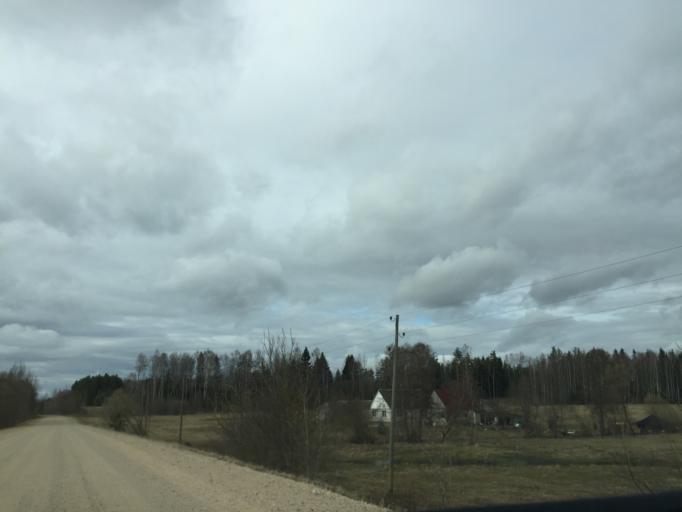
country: LV
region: Daugavpils
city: Daugavpils
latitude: 55.9548
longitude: 26.6956
